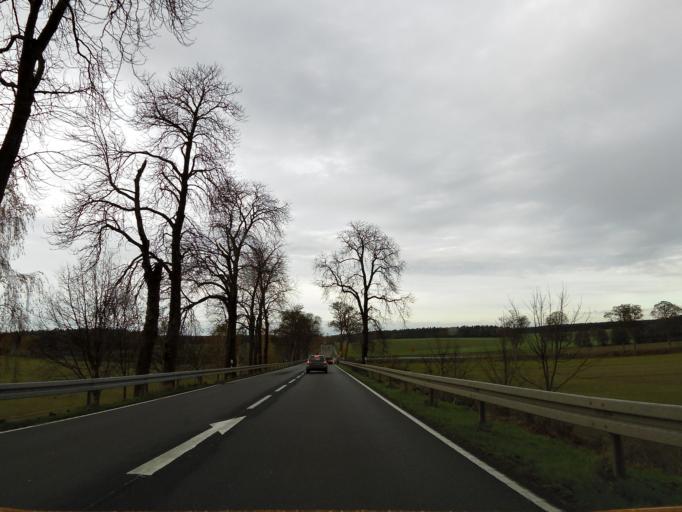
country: DE
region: Saxony-Anhalt
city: Kalbe
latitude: 52.6467
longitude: 11.2992
